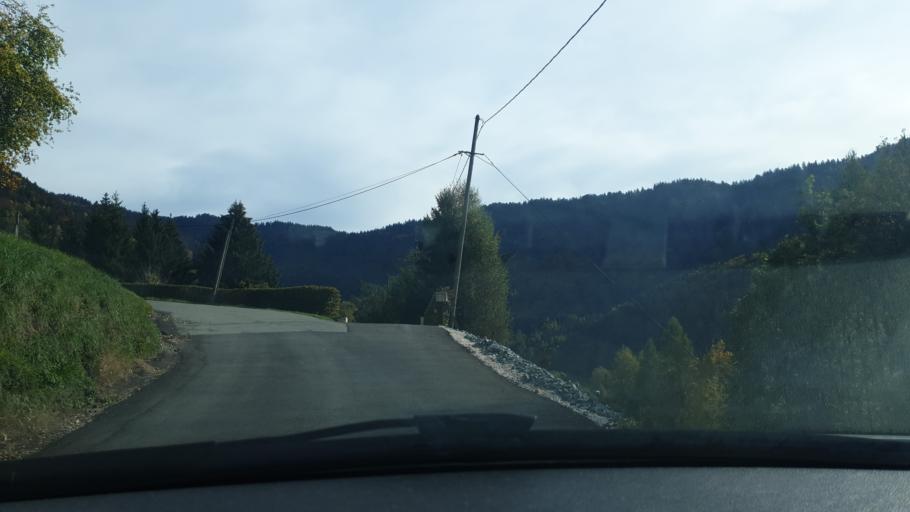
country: FR
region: Rhone-Alpes
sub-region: Departement de la Savoie
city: Aiton
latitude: 45.5011
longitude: 6.2322
